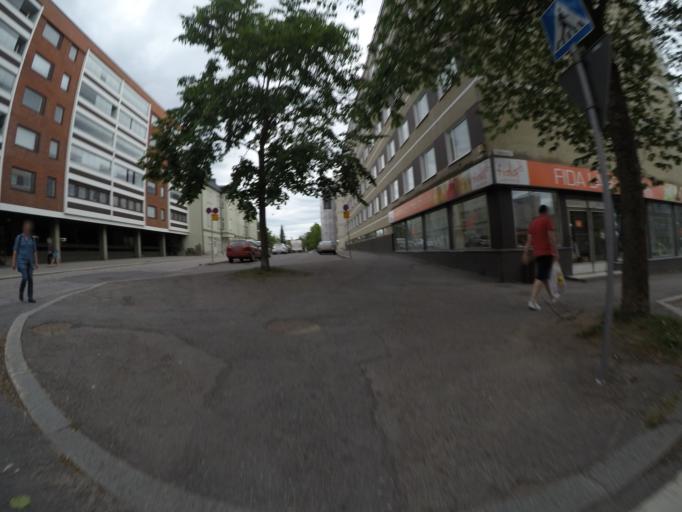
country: FI
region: Haeme
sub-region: Haemeenlinna
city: Haemeenlinna
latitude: 60.9960
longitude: 24.4700
